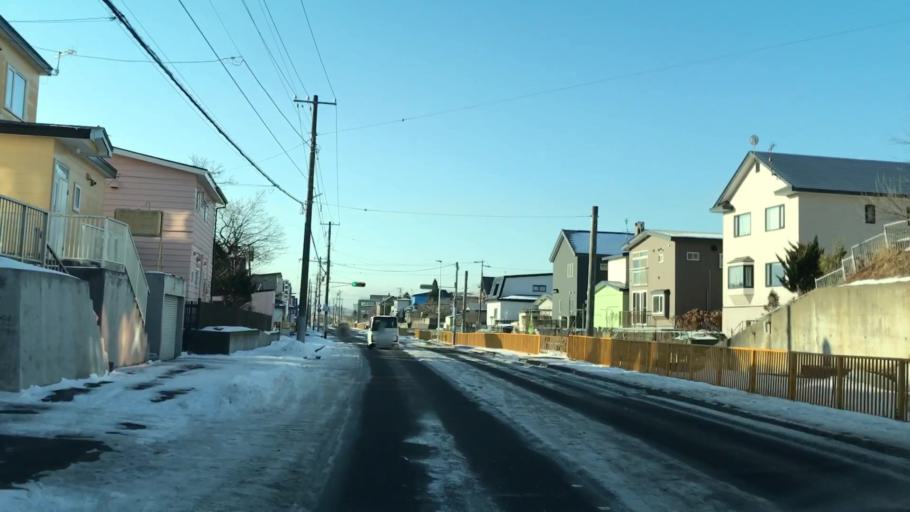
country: JP
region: Hokkaido
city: Muroran
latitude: 42.3691
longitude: 141.0508
